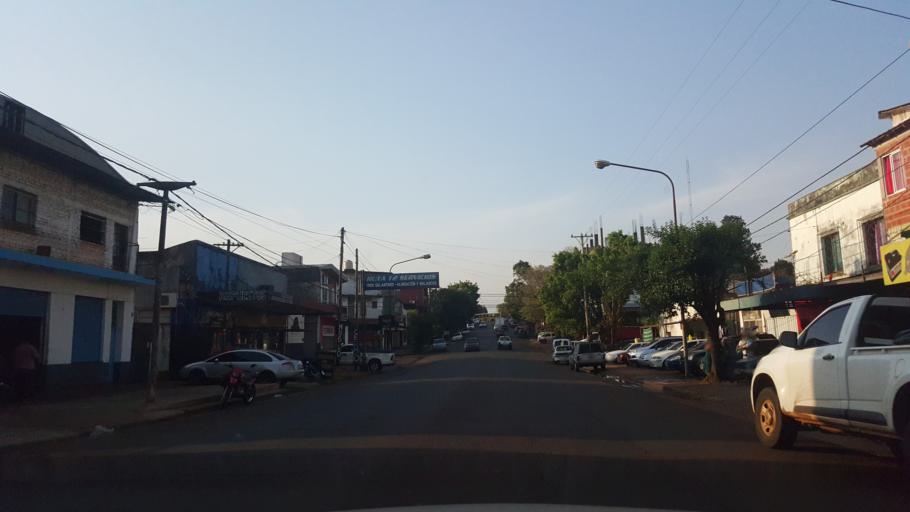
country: AR
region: Misiones
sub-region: Departamento de Capital
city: Posadas
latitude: -27.4026
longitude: -55.9100
